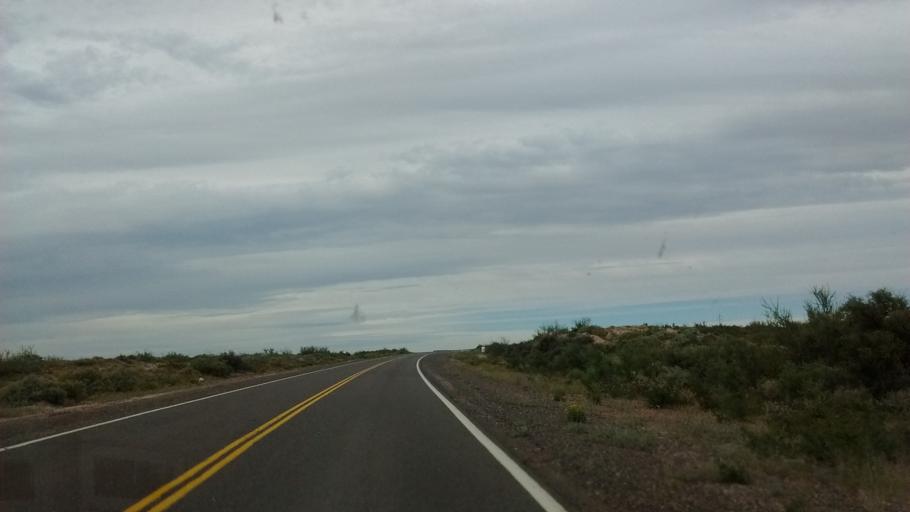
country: AR
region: Rio Negro
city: Catriel
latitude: -38.1253
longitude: -67.9322
